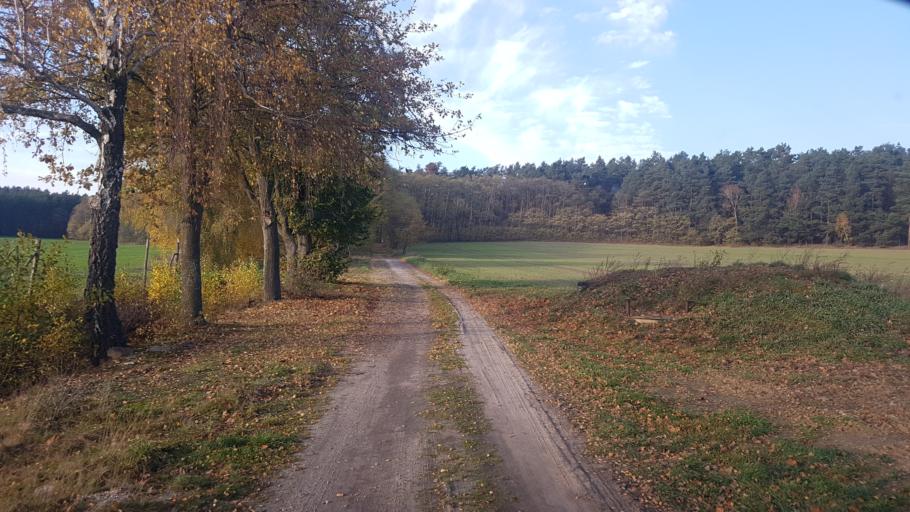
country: DE
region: Brandenburg
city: Calau
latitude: 51.6919
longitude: 13.9657
